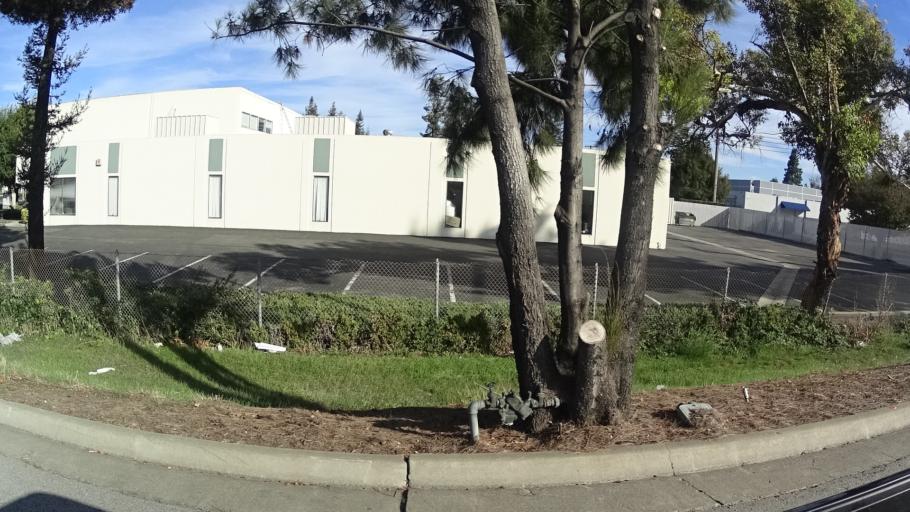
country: US
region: California
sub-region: Santa Clara County
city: Santa Clara
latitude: 37.3689
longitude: -121.9651
